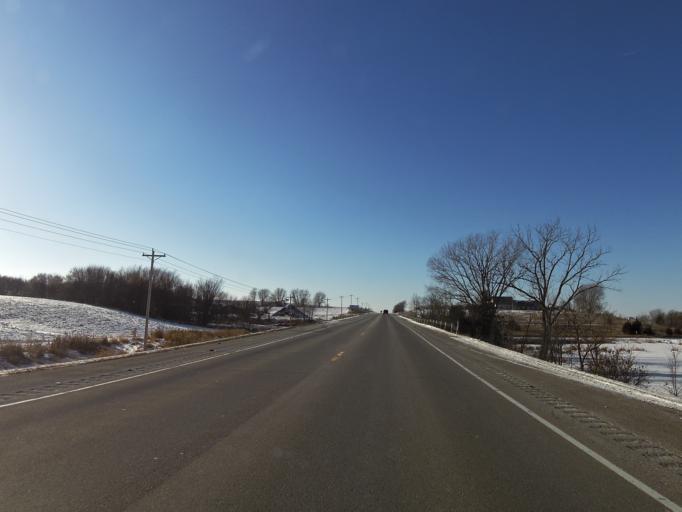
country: US
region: Minnesota
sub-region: Le Sueur County
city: New Prague
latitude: 44.5437
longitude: -93.5147
